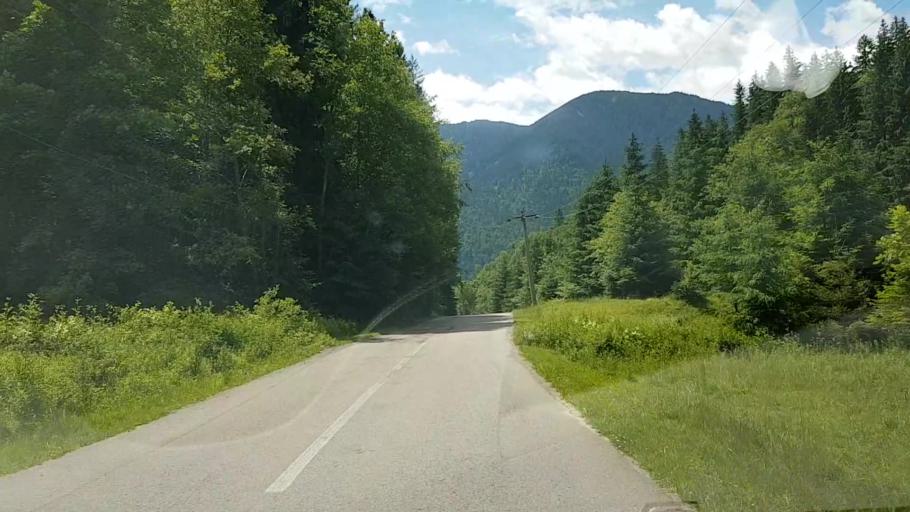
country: RO
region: Suceava
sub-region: Comuna Crucea
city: Crucea
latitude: 47.4089
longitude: 25.5785
